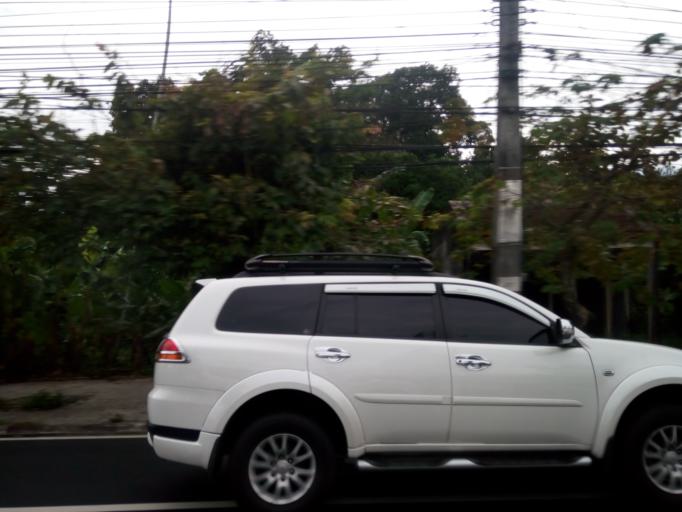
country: TH
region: Phuket
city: Ban Ko Kaeo
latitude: 7.9741
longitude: 98.3690
